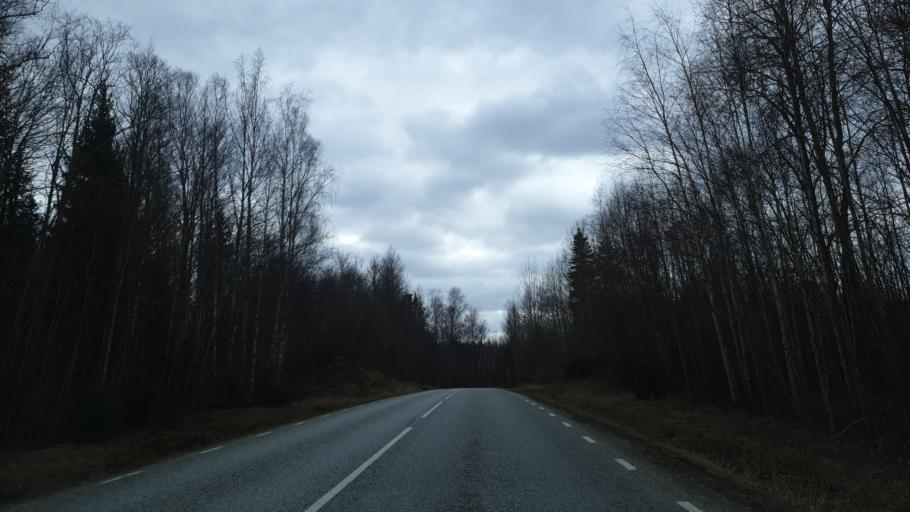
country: SE
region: OErebro
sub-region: Nora Kommun
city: As
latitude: 59.6007
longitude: 14.9220
